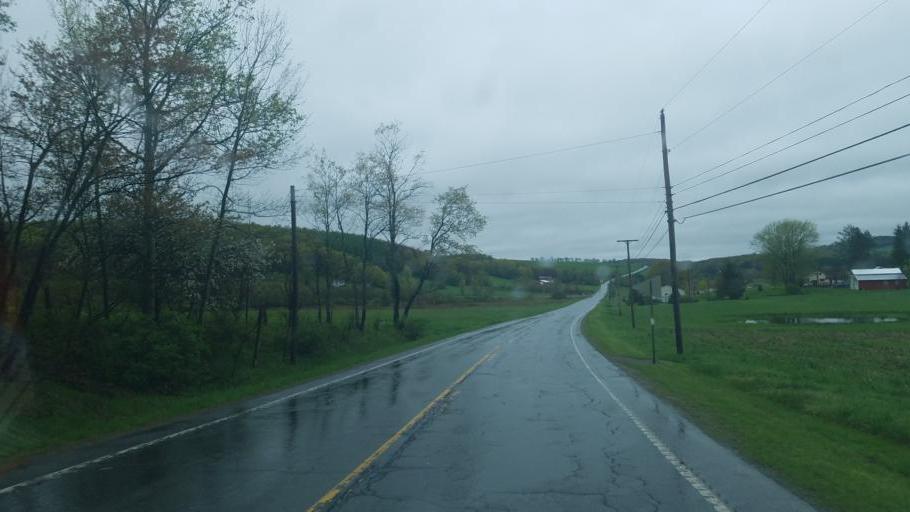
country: US
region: Pennsylvania
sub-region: Potter County
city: Galeton
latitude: 41.8951
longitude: -77.7851
